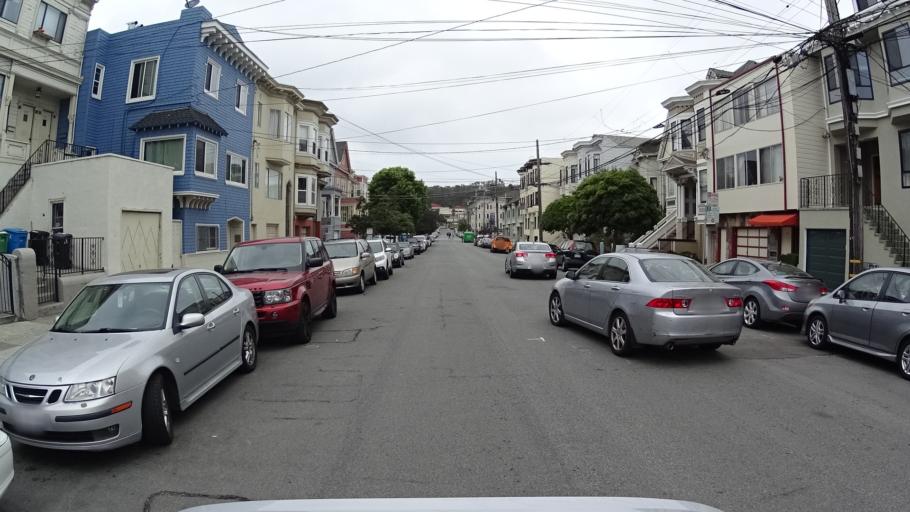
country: US
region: California
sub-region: San Francisco County
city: San Francisco
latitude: 37.7838
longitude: -122.4624
